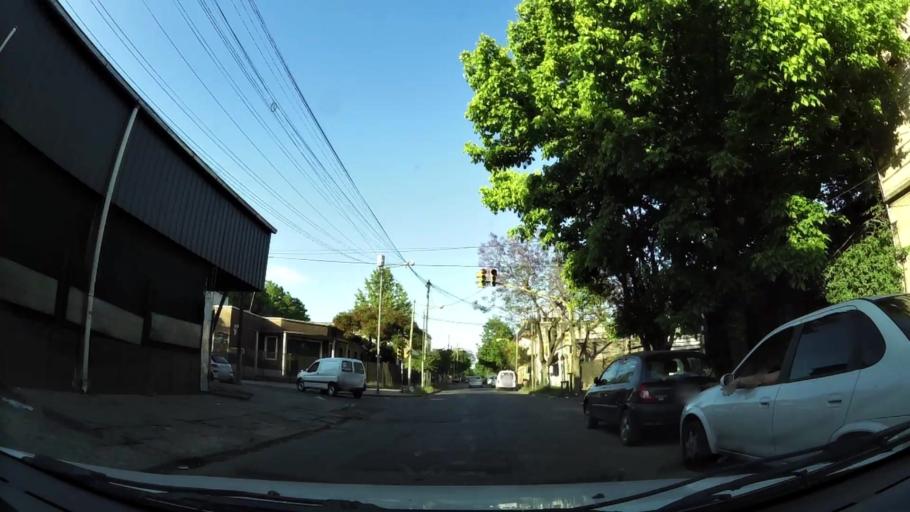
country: AR
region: Buenos Aires
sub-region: Partido de General San Martin
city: General San Martin
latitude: -34.5599
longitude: -58.5630
